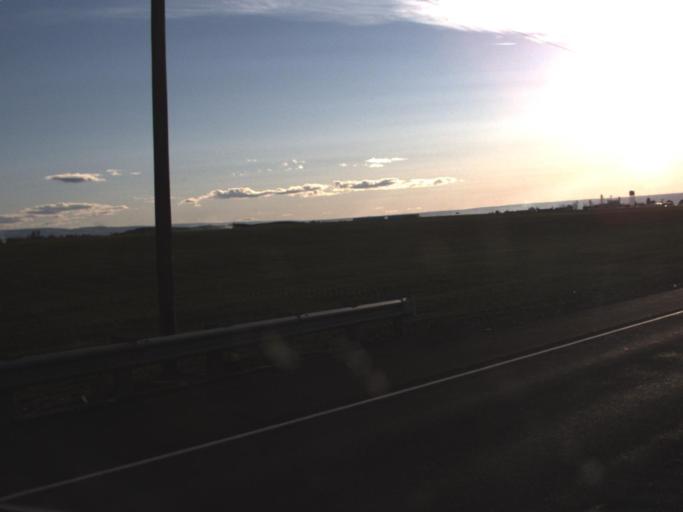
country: US
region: Washington
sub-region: Walla Walla County
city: Walla Walla East
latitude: 46.1024
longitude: -118.2446
